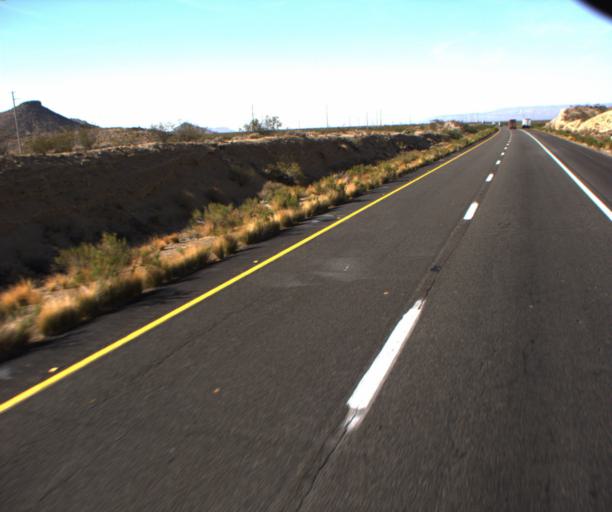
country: US
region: Arizona
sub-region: Mohave County
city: Kingman
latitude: 35.1189
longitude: -114.1131
